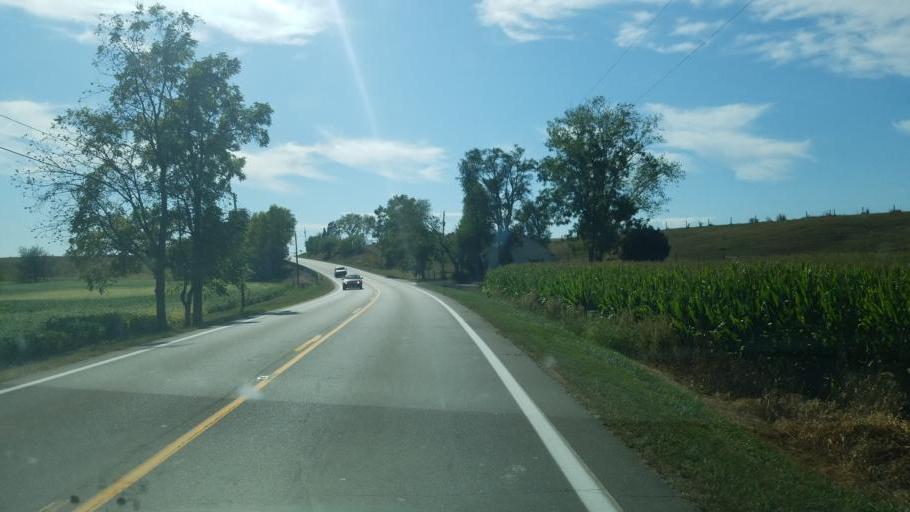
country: US
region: Ohio
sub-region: Clark County
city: Northridge
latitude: 40.0205
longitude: -83.6698
